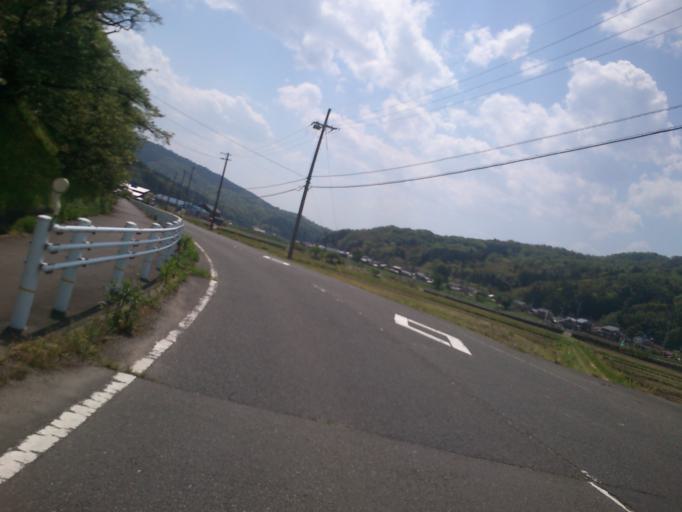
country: JP
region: Kyoto
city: Miyazu
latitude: 35.7133
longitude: 135.1093
